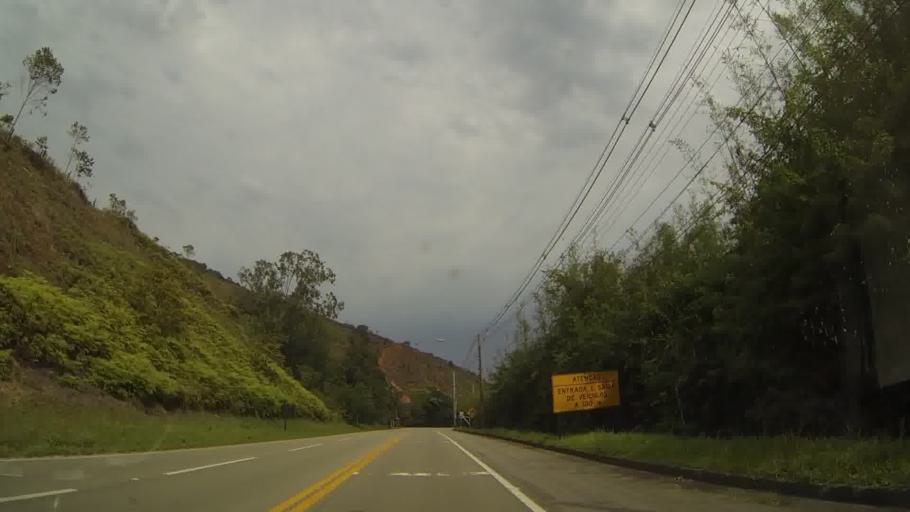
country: BR
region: Sao Paulo
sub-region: Sao Sebastiao
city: Sao Sebastiao
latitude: -23.8094
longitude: -45.5392
